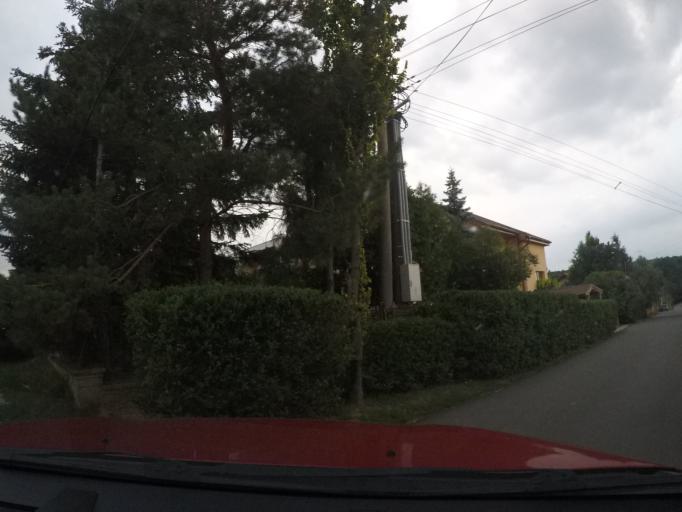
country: SK
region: Kosicky
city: Kosice
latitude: 48.6927
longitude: 21.2094
